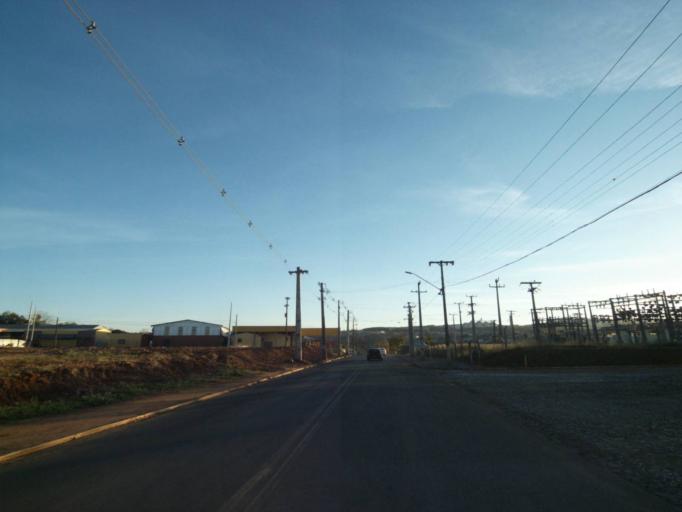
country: BR
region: Parana
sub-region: Tibagi
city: Tibagi
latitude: -24.5101
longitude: -50.4164
